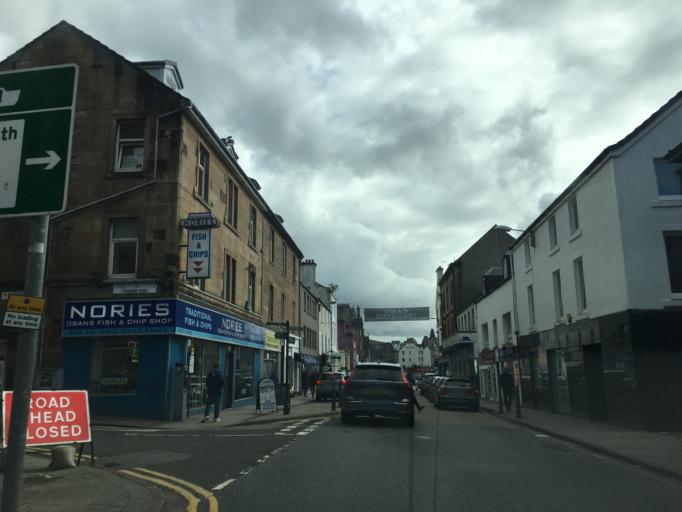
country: GB
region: Scotland
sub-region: Argyll and Bute
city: Oban
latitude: 56.4157
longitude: -5.4729
